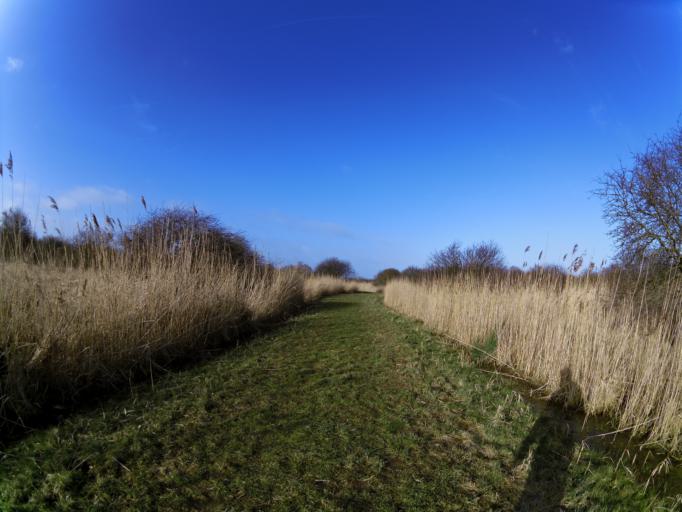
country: NL
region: South Holland
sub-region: Gemeente Rotterdam
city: Hoek van Holland
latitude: 51.9238
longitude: 4.0853
